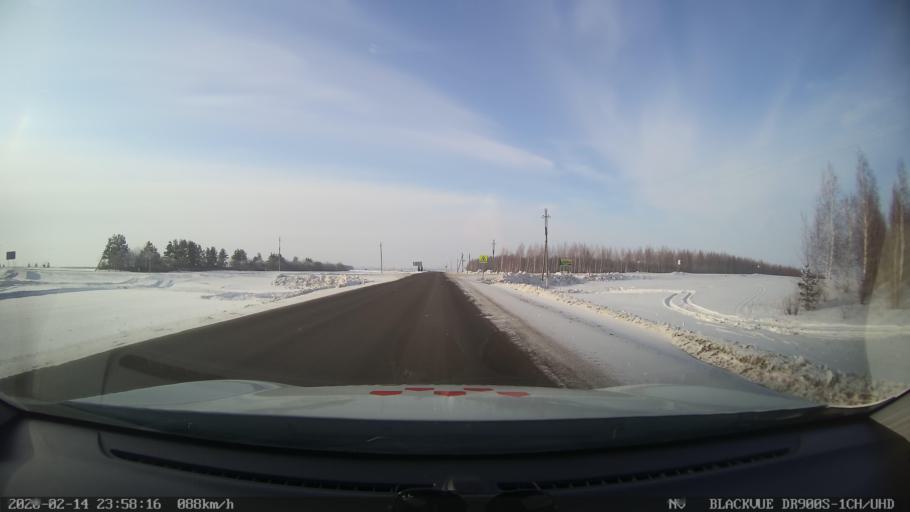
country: RU
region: Tatarstan
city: Kuybyshevskiy Zaton
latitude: 55.3398
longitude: 49.0909
